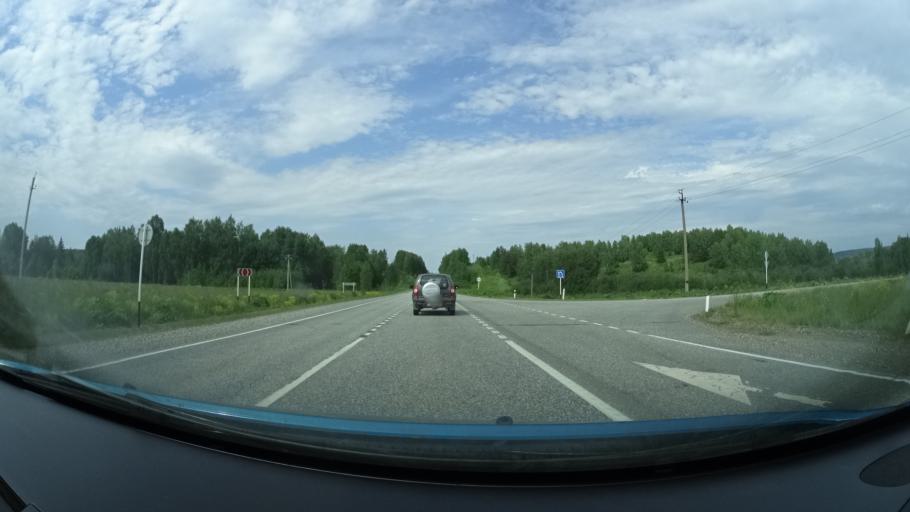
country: RU
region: Perm
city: Osa
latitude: 57.1583
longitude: 55.5302
